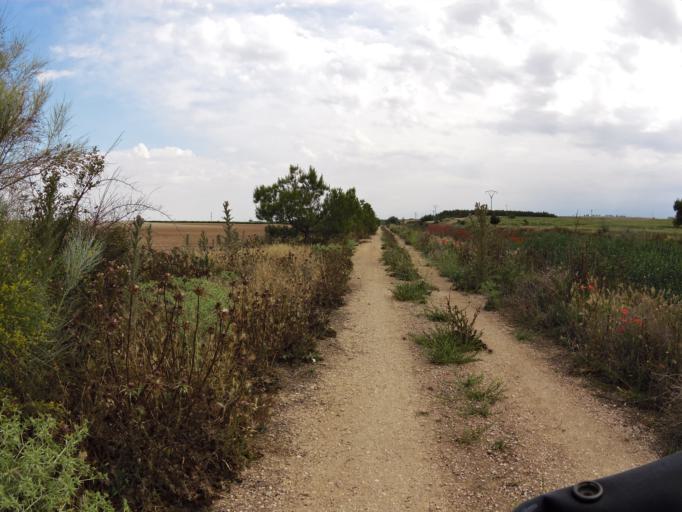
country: ES
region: Castille-La Mancha
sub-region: Provincia de Albacete
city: Albacete
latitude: 39.0499
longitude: -1.7589
